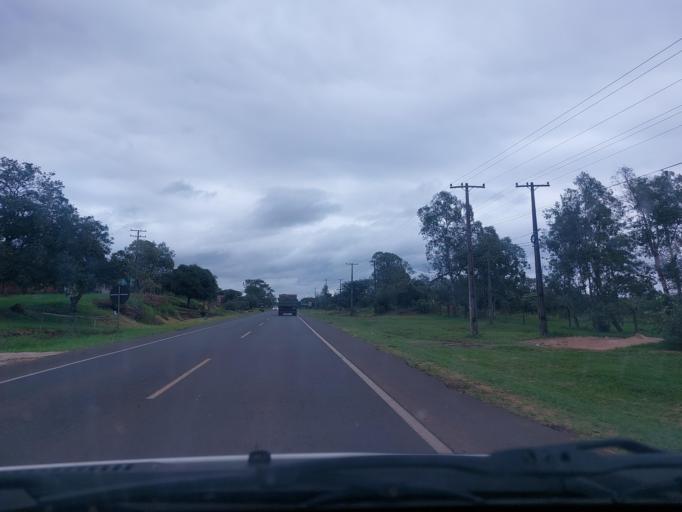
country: PY
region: San Pedro
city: Guayaybi
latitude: -24.6743
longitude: -56.4058
